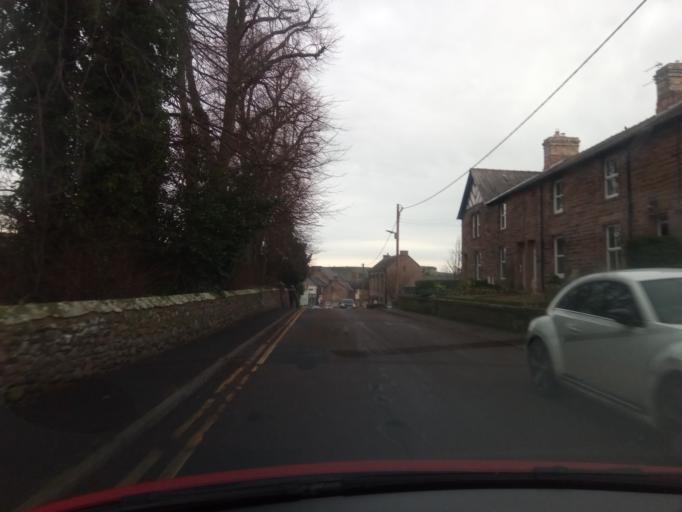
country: GB
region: England
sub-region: Northumberland
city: Wooler
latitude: 55.5476
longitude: -2.0194
